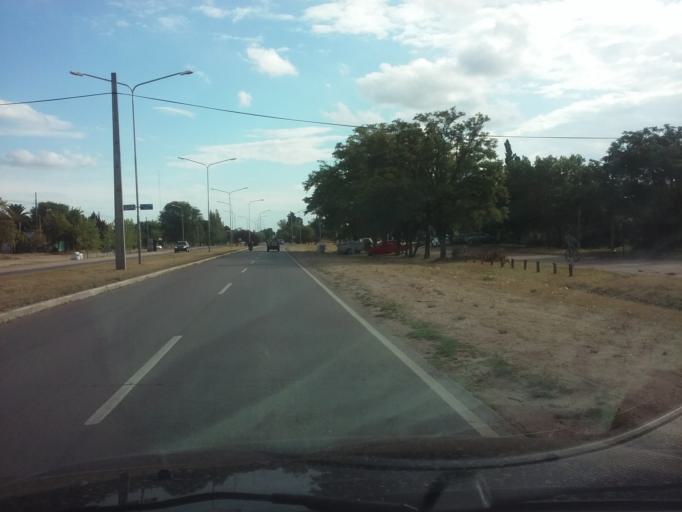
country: AR
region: La Pampa
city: Santa Rosa
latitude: -36.6371
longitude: -64.3185
